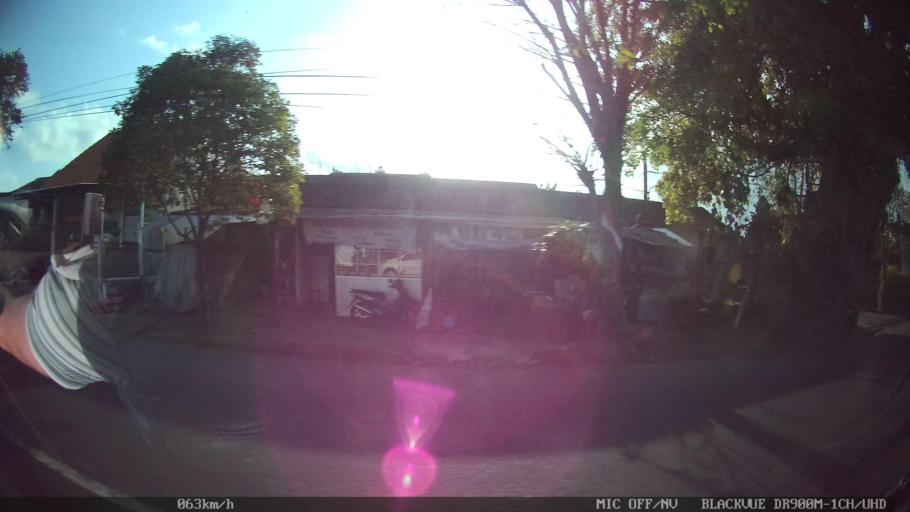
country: ID
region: Bali
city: Banjar Batur
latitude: -8.5992
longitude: 115.2144
